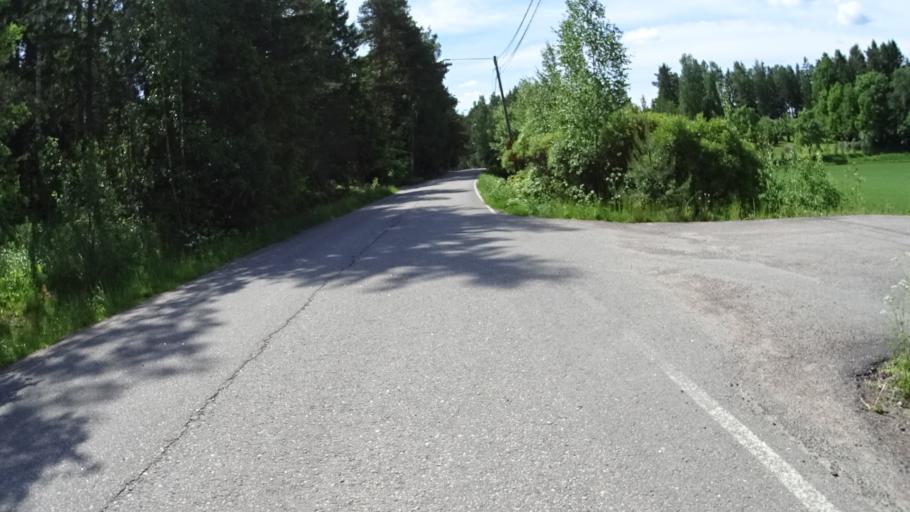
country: FI
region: Uusimaa
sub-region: Helsinki
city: Espoo
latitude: 60.2852
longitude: 24.6770
